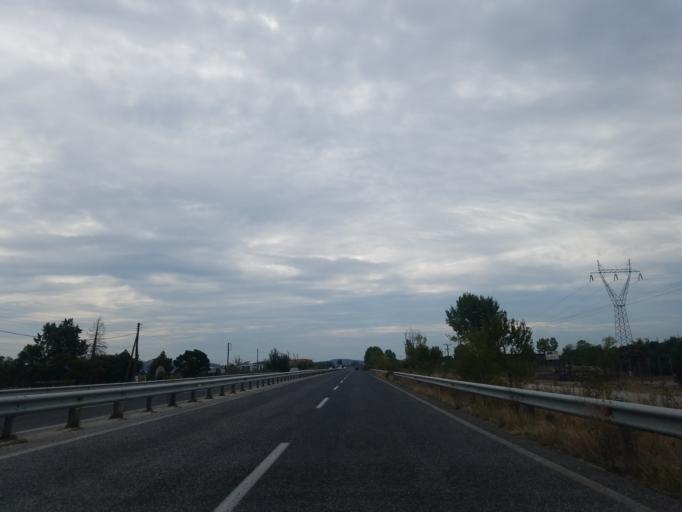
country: GR
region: Thessaly
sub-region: Trikala
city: Vasiliki
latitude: 39.6083
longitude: 21.7233
